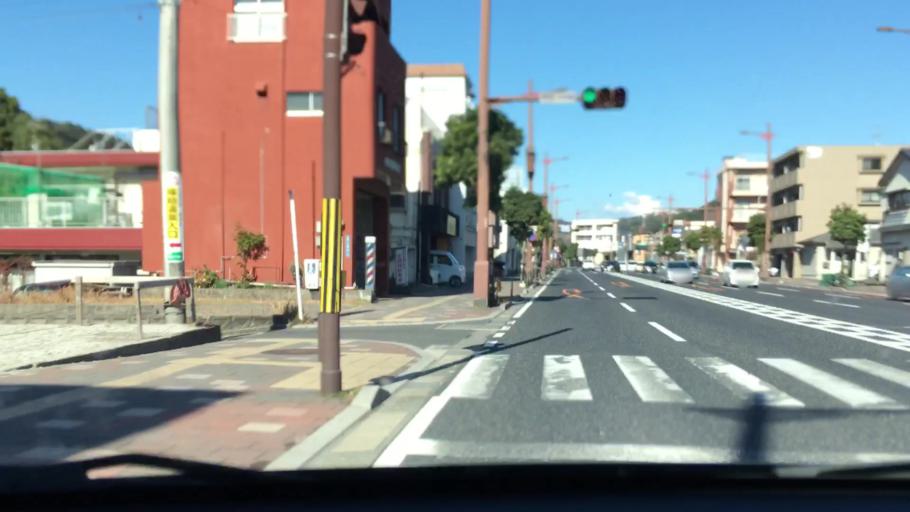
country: JP
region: Kagoshima
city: Kagoshima-shi
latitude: 31.6191
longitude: 130.5267
